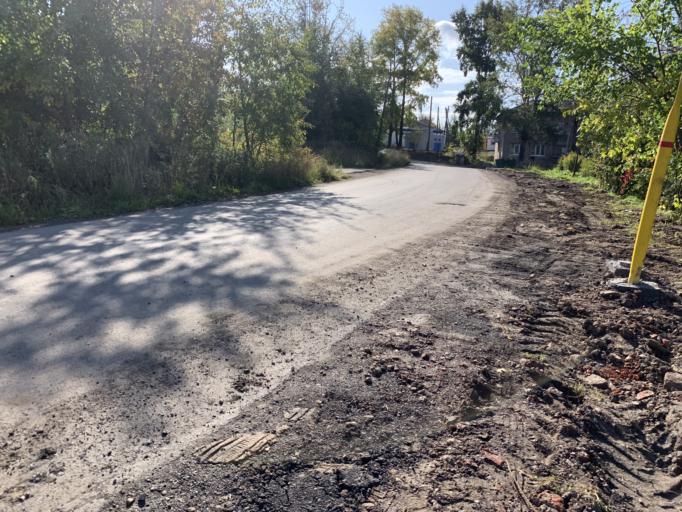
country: RU
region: Perm
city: Gubakha
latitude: 58.8440
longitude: 57.5538
